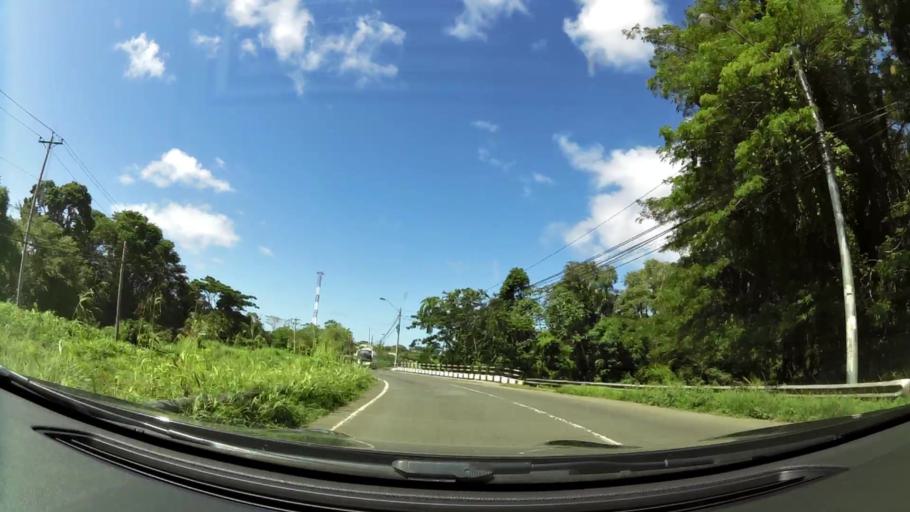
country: TT
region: Tobago
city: Scarborough
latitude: 11.2161
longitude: -60.7713
